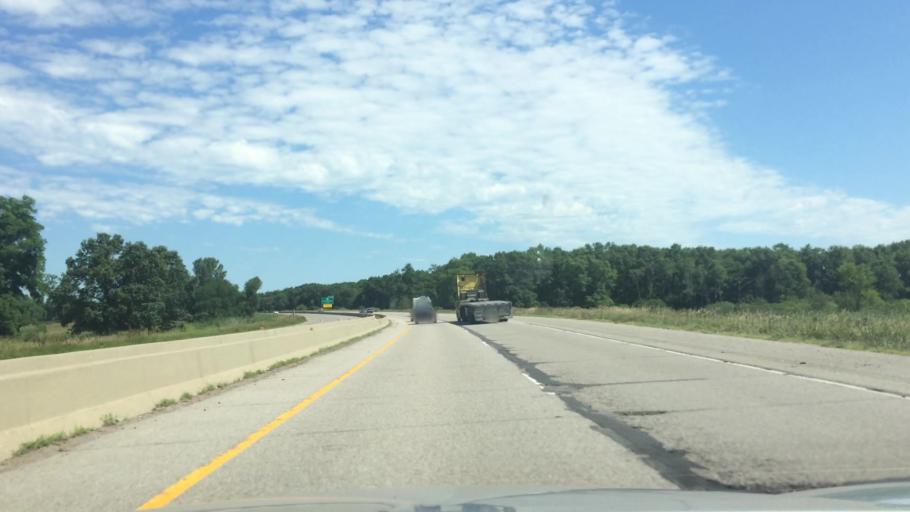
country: US
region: Wisconsin
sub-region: Marquette County
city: Westfield
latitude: 43.7369
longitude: -89.4837
